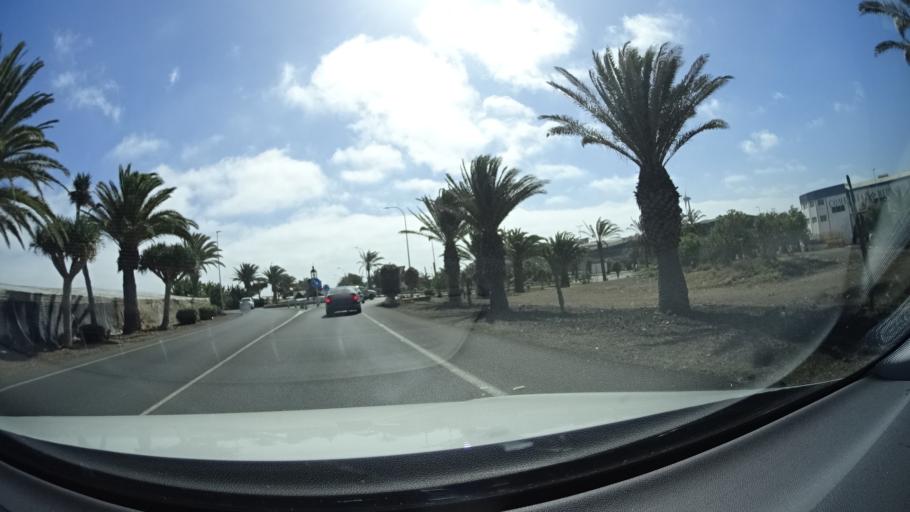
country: ES
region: Canary Islands
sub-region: Provincia de Las Palmas
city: Cruce de Arinaga
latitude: 27.8633
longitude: -15.4062
